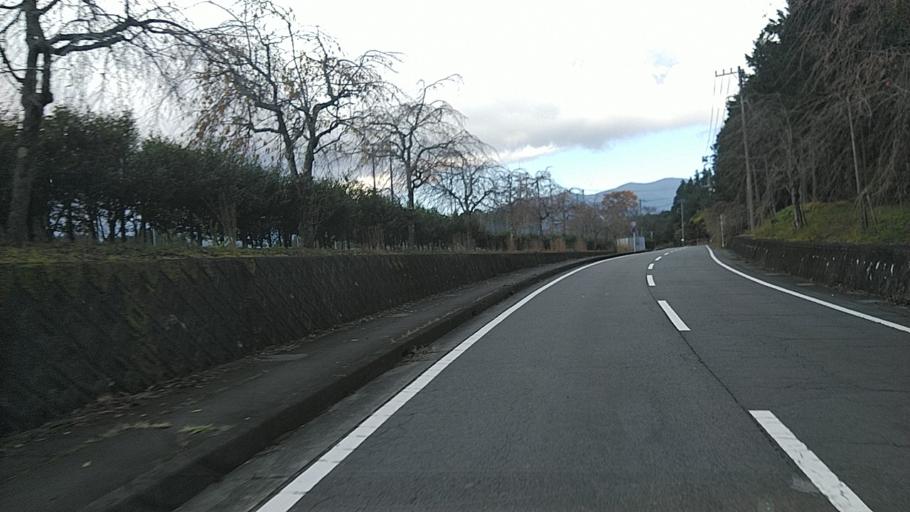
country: JP
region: Shizuoka
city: Gotemba
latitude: 35.3196
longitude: 138.9592
